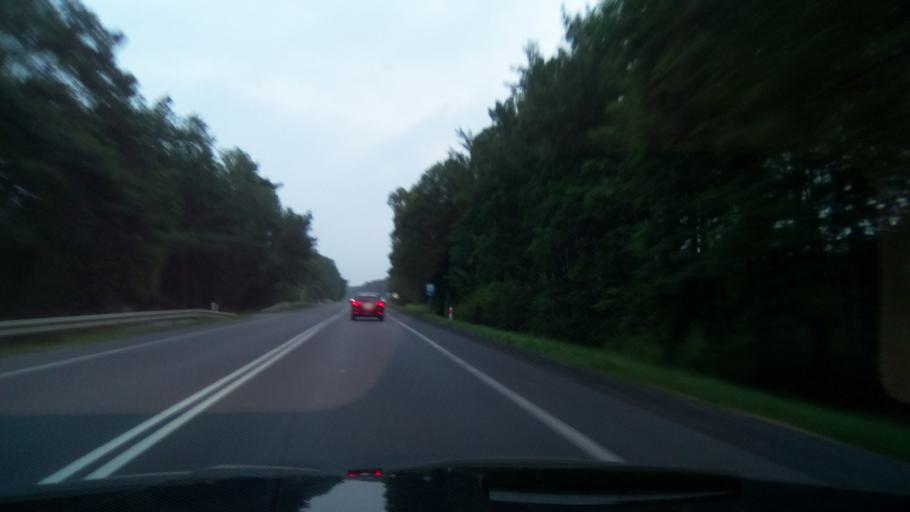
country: PL
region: Greater Poland Voivodeship
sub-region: Powiat poznanski
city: Kostrzyn
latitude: 52.4689
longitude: 17.1825
